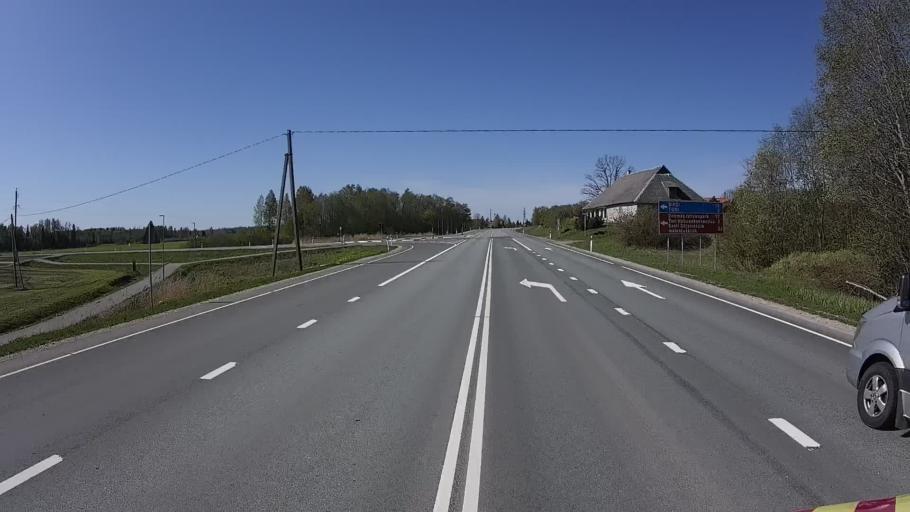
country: EE
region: Paernumaa
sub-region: Tootsi vald
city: Tootsi
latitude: 58.5054
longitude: 24.7965
